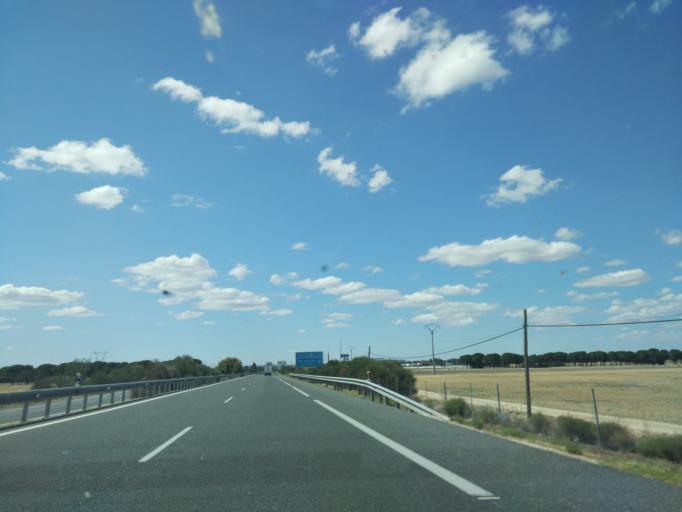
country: ES
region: Castille and Leon
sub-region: Provincia de Valladolid
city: San Vicente del Palacio
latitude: 41.2146
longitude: -4.8373
